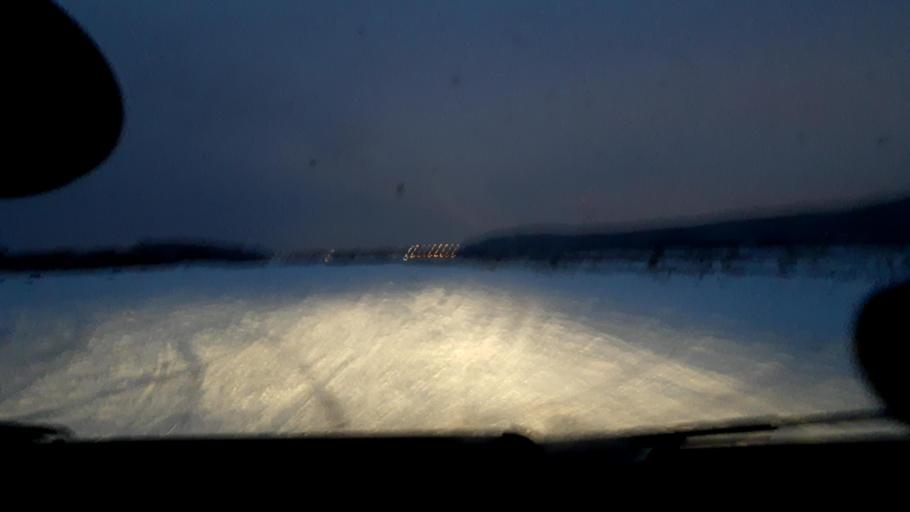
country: RU
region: Bashkortostan
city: Ufa
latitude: 54.8264
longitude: 56.1641
